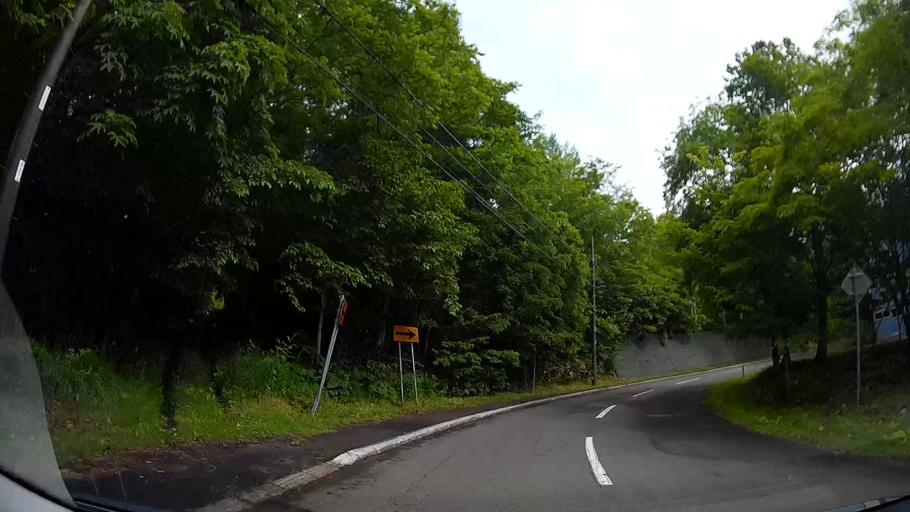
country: JP
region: Hokkaido
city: Sapporo
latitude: 42.9432
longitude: 141.1537
